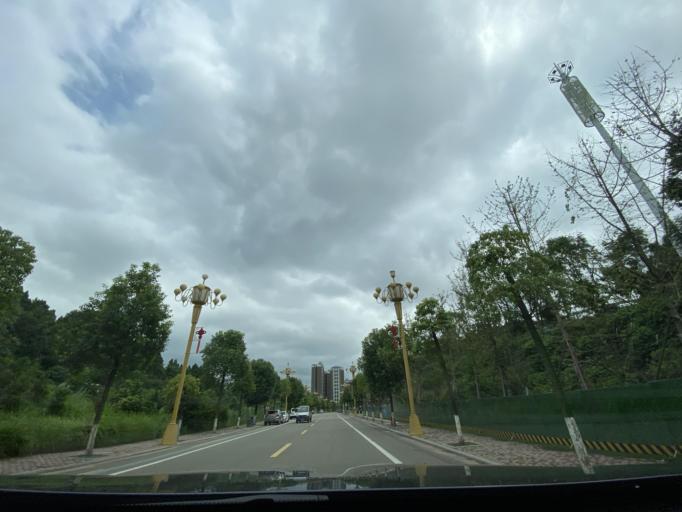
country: CN
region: Sichuan
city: Jiancheng
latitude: 30.4061
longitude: 104.5546
